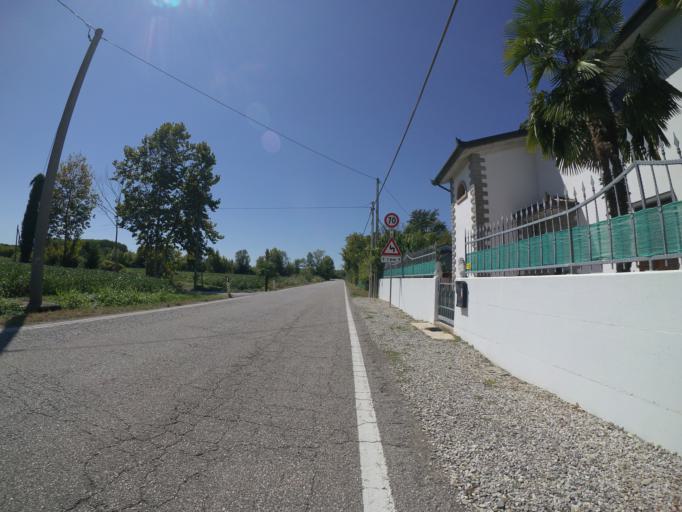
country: IT
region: Friuli Venezia Giulia
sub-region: Provincia di Udine
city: Rivignano
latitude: 45.8658
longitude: 13.0307
